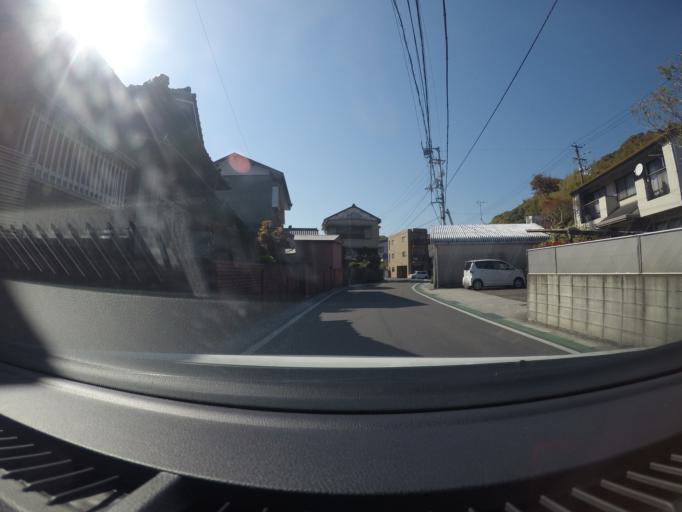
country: JP
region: Kochi
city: Kochi-shi
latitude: 33.5427
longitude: 133.5741
